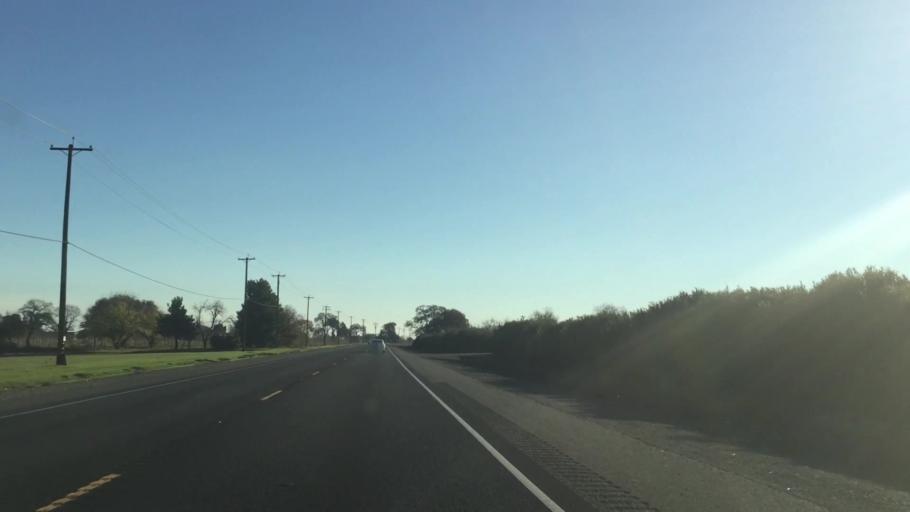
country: US
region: California
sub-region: Sutter County
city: Live Oak
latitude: 39.3407
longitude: -121.5996
